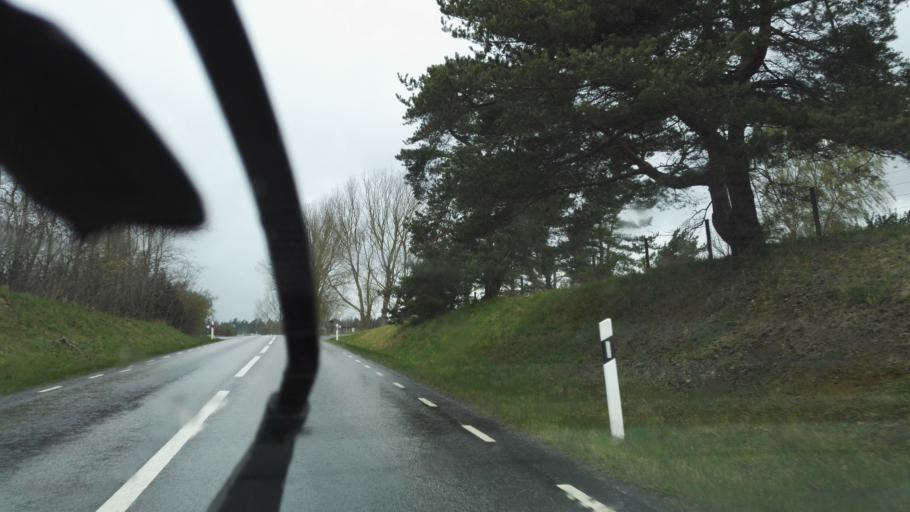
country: SE
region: Skane
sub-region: Simrishamns Kommun
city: Kivik
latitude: 55.7094
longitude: 14.1715
